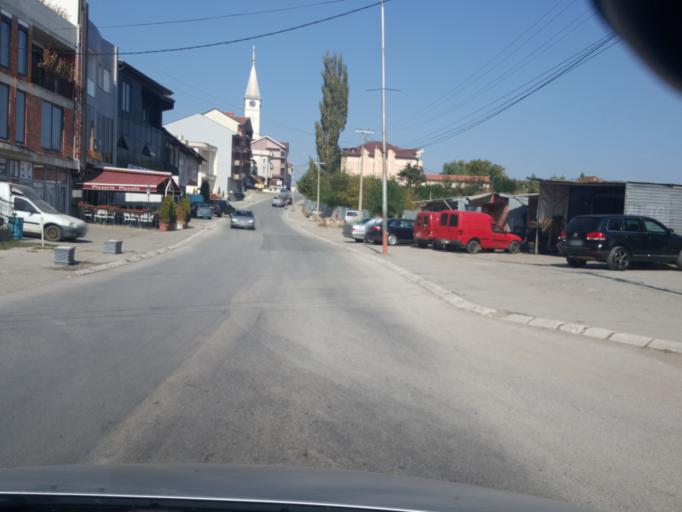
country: XK
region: Gjakova
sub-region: Komuna e Gjakoves
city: Gjakove
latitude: 42.3712
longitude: 20.4221
